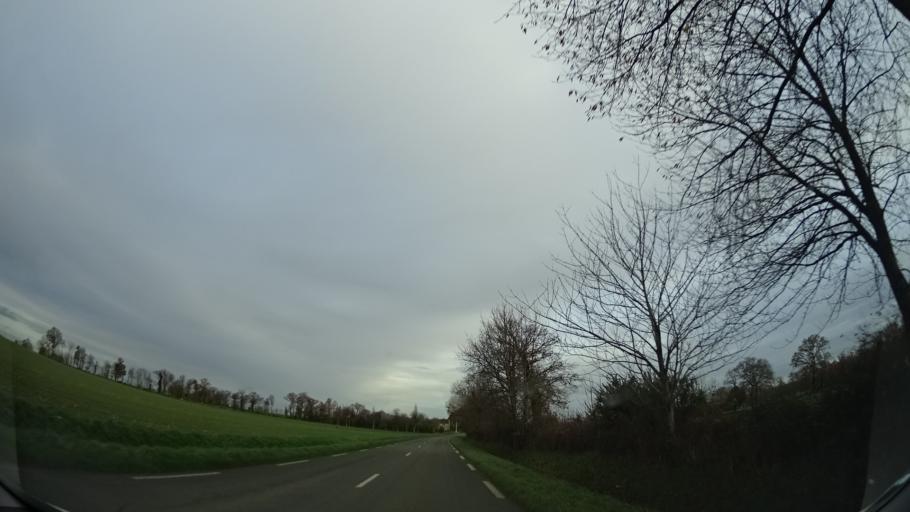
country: FR
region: Brittany
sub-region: Departement des Cotes-d'Armor
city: Evran
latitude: 48.3612
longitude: -1.9701
